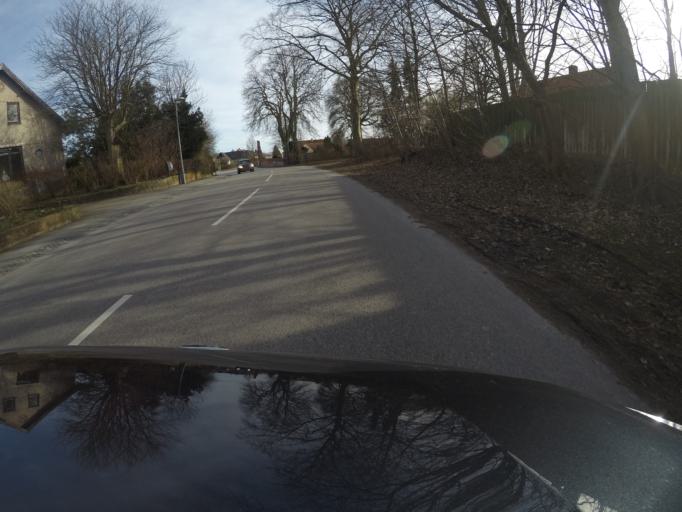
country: DK
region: Capital Region
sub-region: Halsnaes Kommune
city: Liseleje
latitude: 55.9841
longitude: 11.9407
